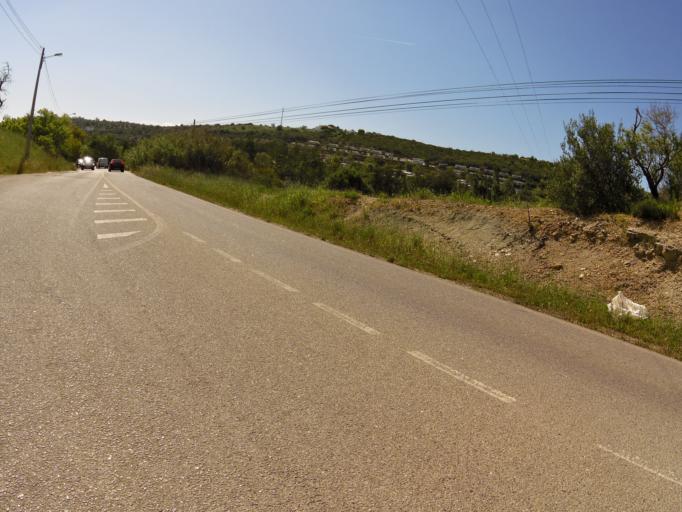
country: PT
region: Faro
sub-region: Lagos
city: Lagos
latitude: 37.1006
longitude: -8.7148
